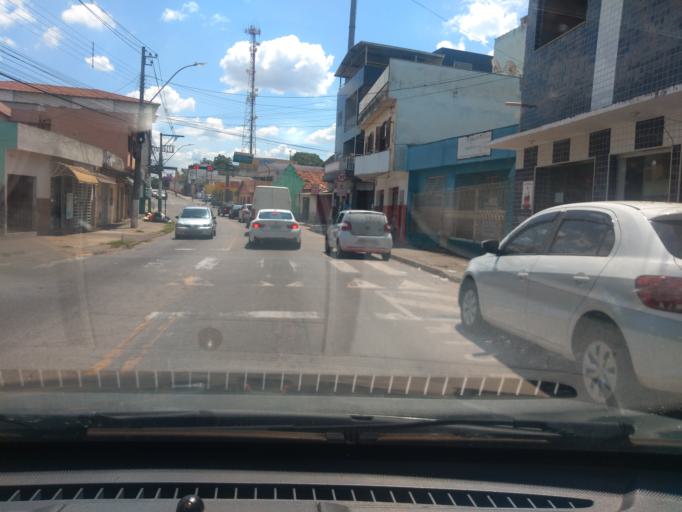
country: BR
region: Minas Gerais
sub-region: Tres Coracoes
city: Tres Coracoes
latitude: -21.6926
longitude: -45.2481
